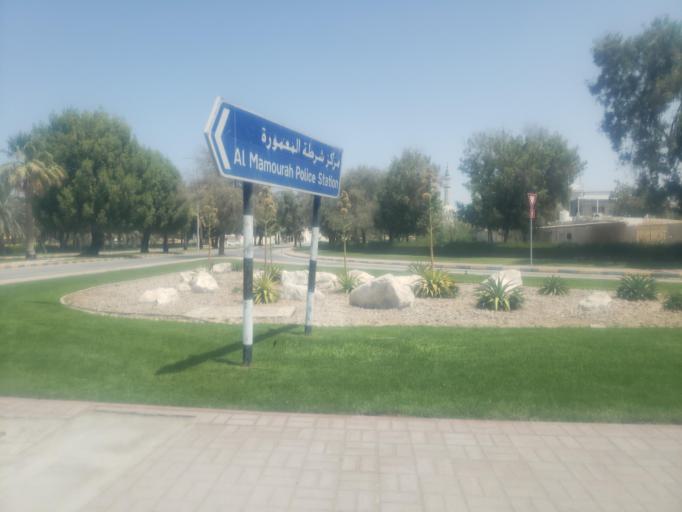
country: AE
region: Ra's al Khaymah
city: Ras al-Khaimah
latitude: 25.8030
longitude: 55.9699
